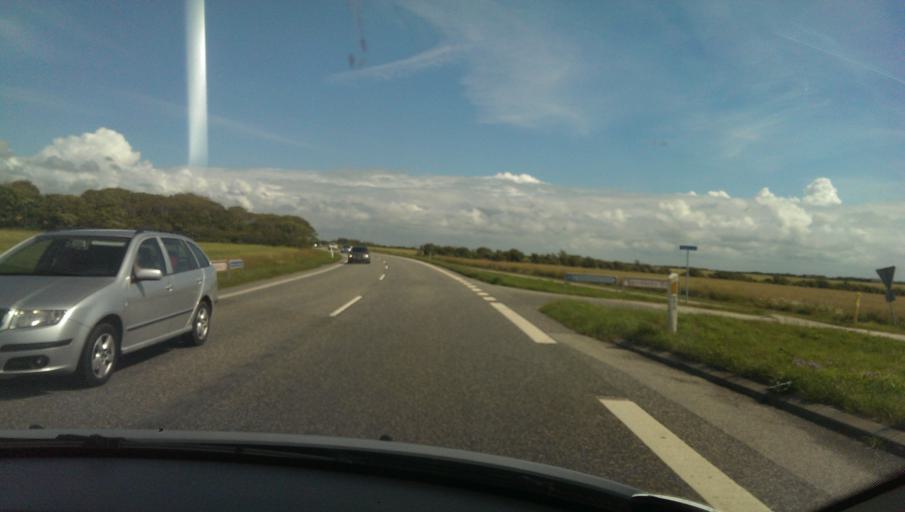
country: DK
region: Central Jutland
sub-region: Ringkobing-Skjern Kommune
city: Ringkobing
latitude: 56.1148
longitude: 8.1753
